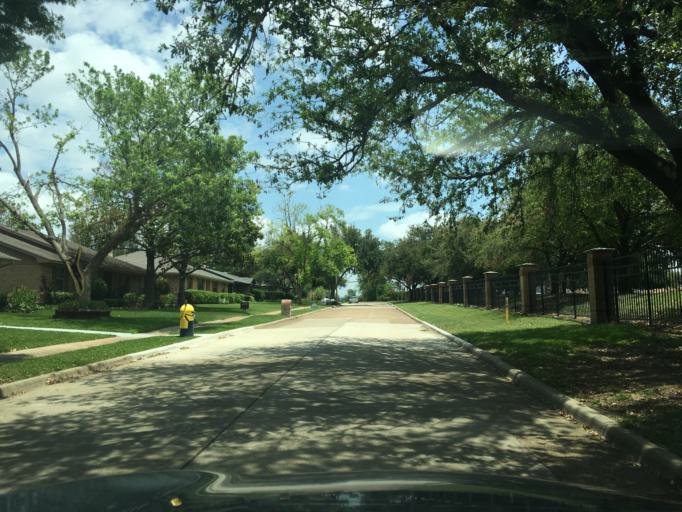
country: US
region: Texas
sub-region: Dallas County
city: Richardson
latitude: 32.9077
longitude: -96.7520
